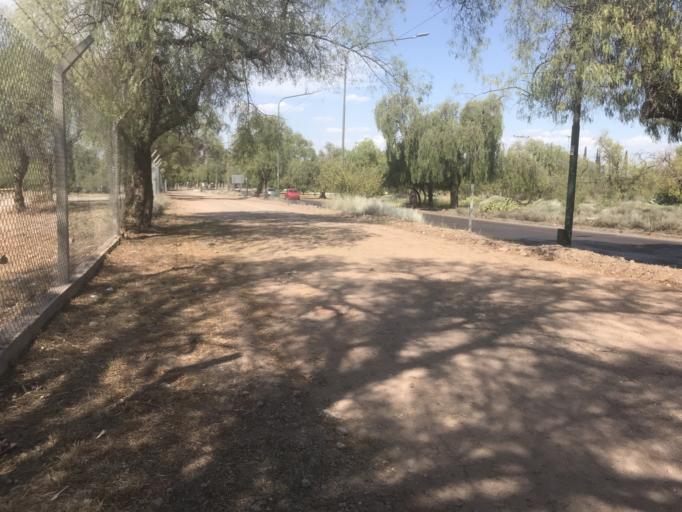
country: AR
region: Mendoza
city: Mendoza
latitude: -32.8823
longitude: -68.8853
